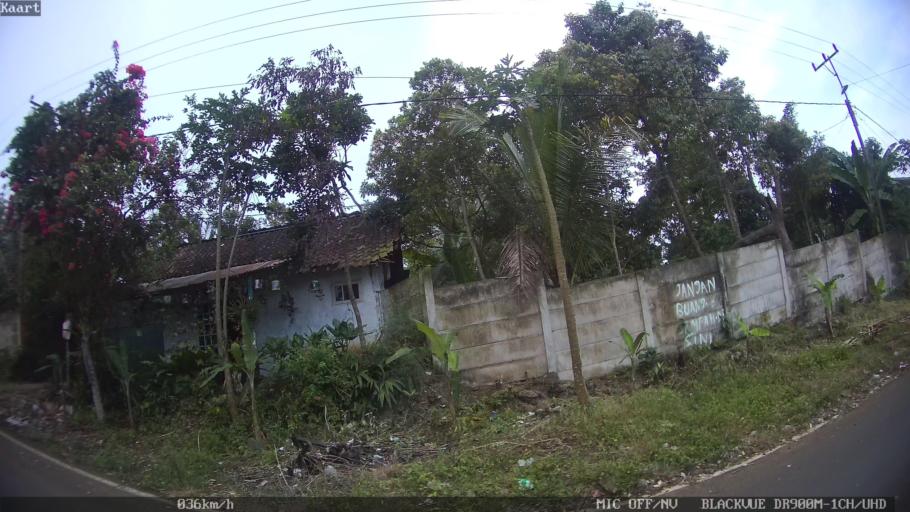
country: ID
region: Lampung
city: Bandarlampung
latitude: -5.4347
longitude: 105.2143
